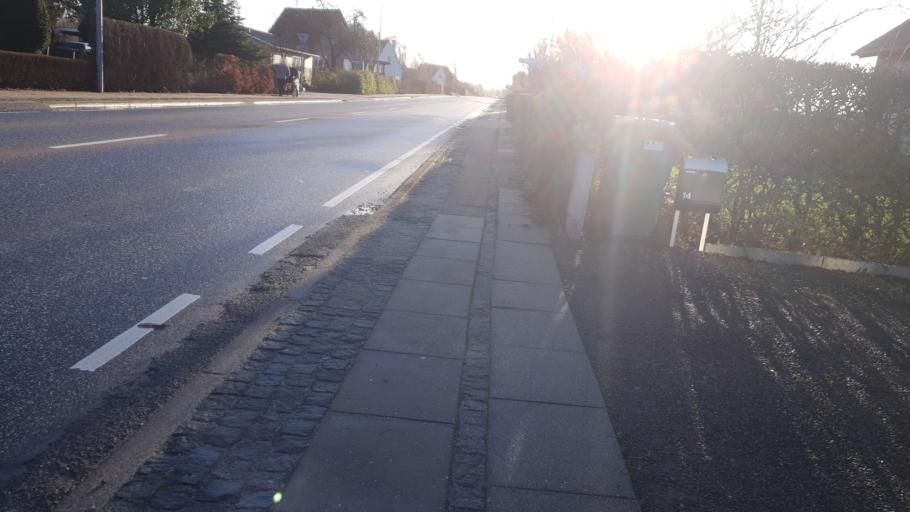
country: DK
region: Central Jutland
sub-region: Hedensted Kommune
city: Hedensted
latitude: 55.8026
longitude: 9.6937
